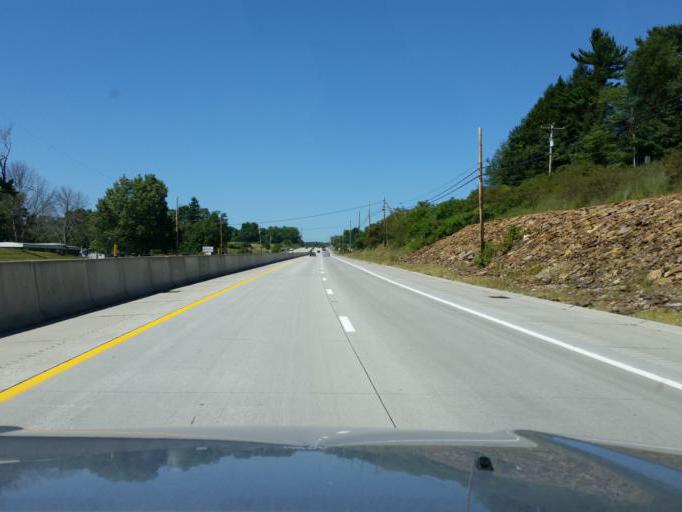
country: US
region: Pennsylvania
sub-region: Indiana County
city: Blairsville
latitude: 40.4292
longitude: -79.2958
